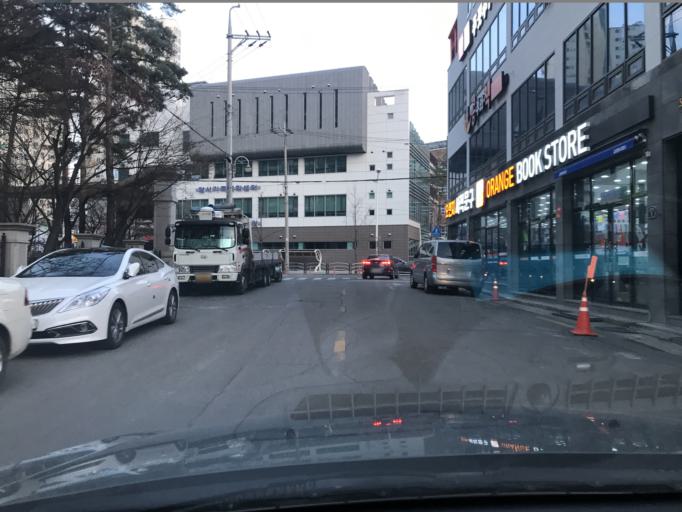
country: KR
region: Daegu
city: Hwawon
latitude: 35.8179
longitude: 128.5182
